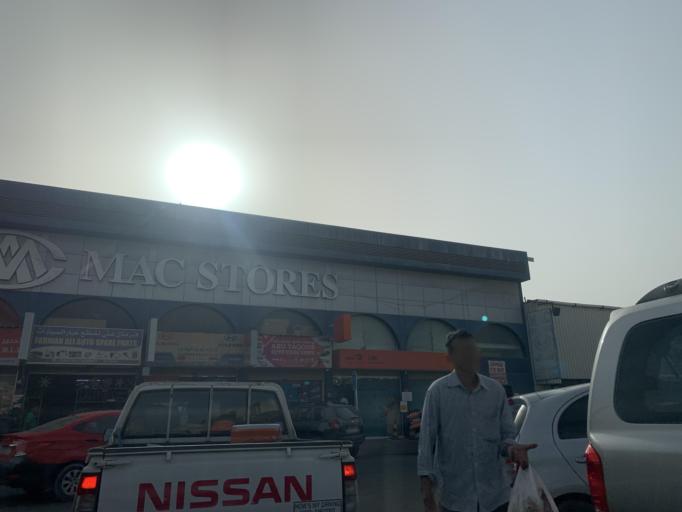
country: BH
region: Northern
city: Madinat `Isa
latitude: 26.1843
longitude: 50.5315
